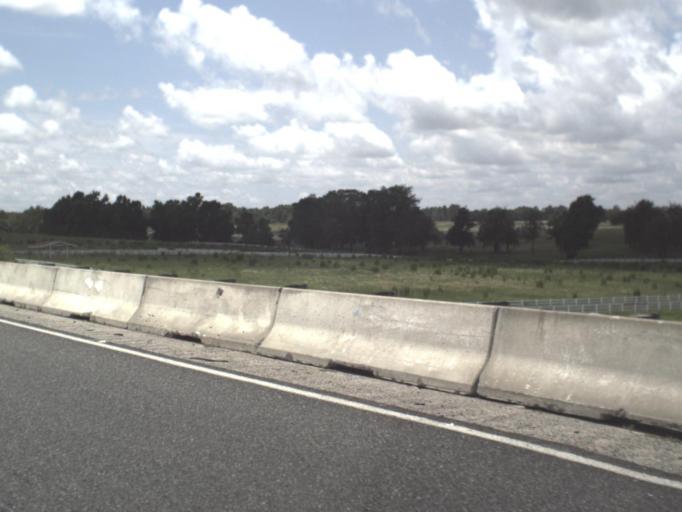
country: US
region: Florida
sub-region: Alachua County
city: High Springs
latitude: 29.7989
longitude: -82.5145
